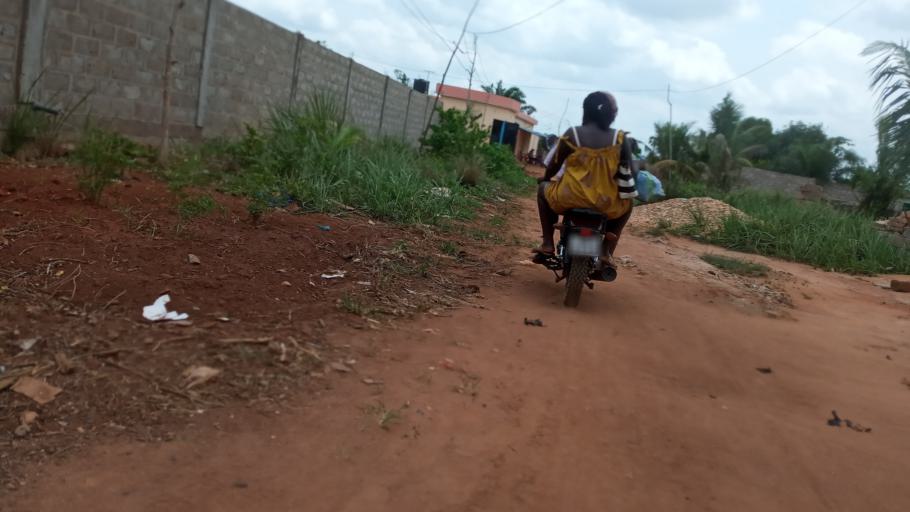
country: TG
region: Maritime
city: Tsevie
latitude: 6.2962
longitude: 1.1309
